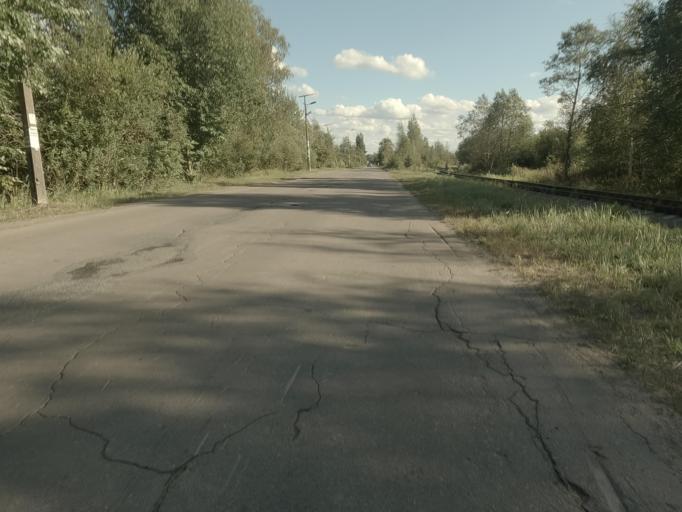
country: RU
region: Leningrad
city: Imeni Morozova
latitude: 59.9666
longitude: 31.0287
